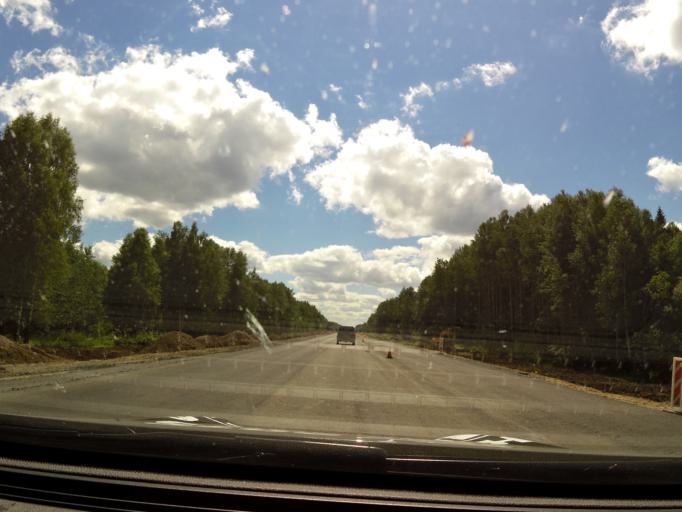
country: RU
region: Vologda
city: Molochnoye
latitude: 59.3648
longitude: 39.6727
